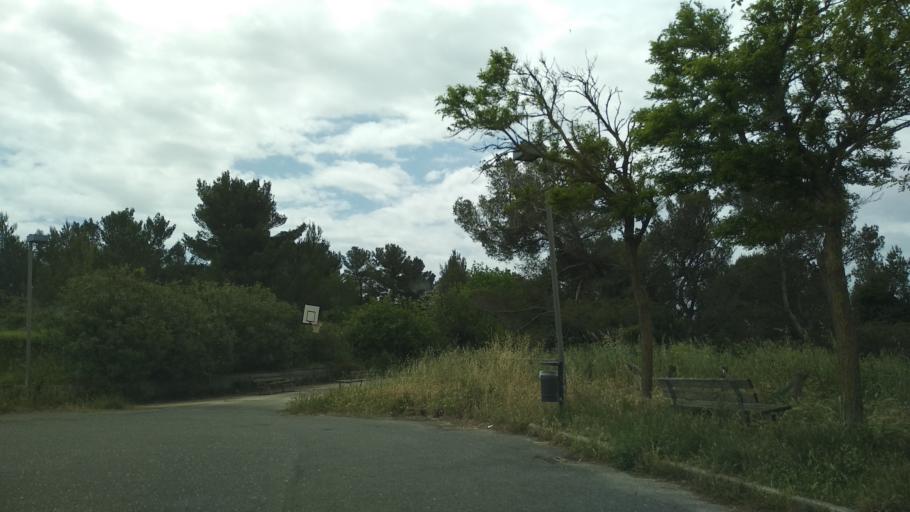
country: IT
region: Tuscany
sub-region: Provincia di Livorno
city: Quercianella
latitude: 43.4858
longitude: 10.3625
